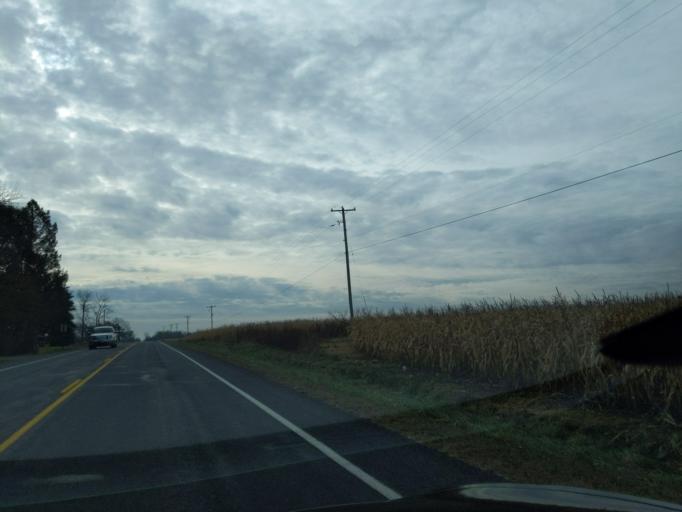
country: US
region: Michigan
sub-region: Ingham County
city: Holt
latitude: 42.5998
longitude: -84.5230
